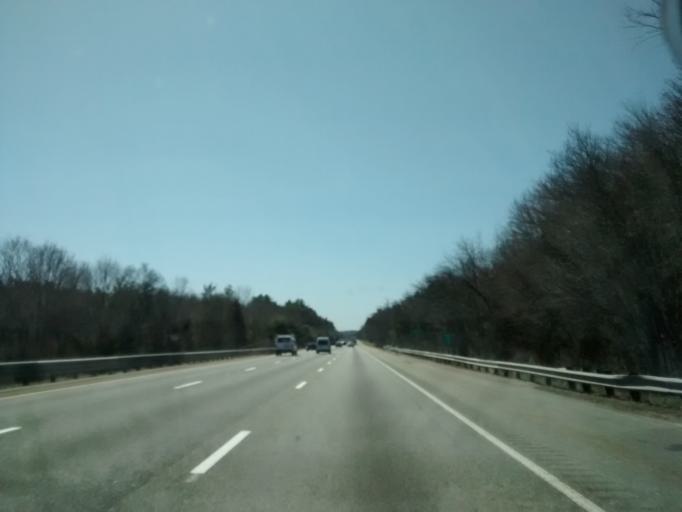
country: US
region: Massachusetts
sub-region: Bristol County
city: Mansfield Center
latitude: 42.0202
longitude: -71.2670
